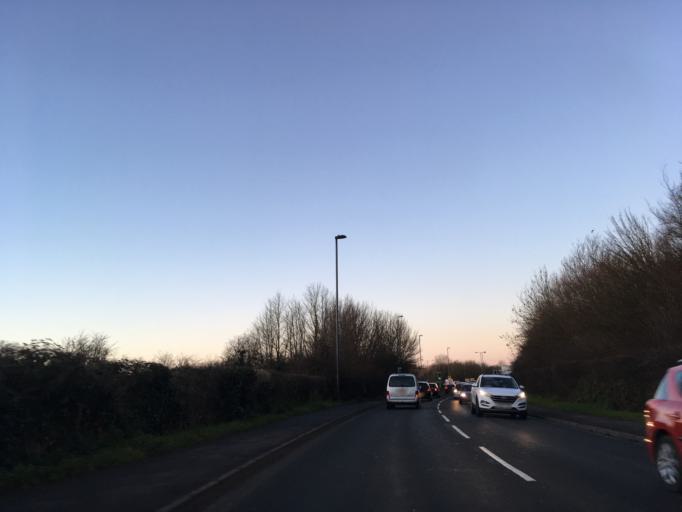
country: GB
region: England
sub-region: South Gloucestershire
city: Stoke Gifford
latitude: 51.5198
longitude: -2.5502
